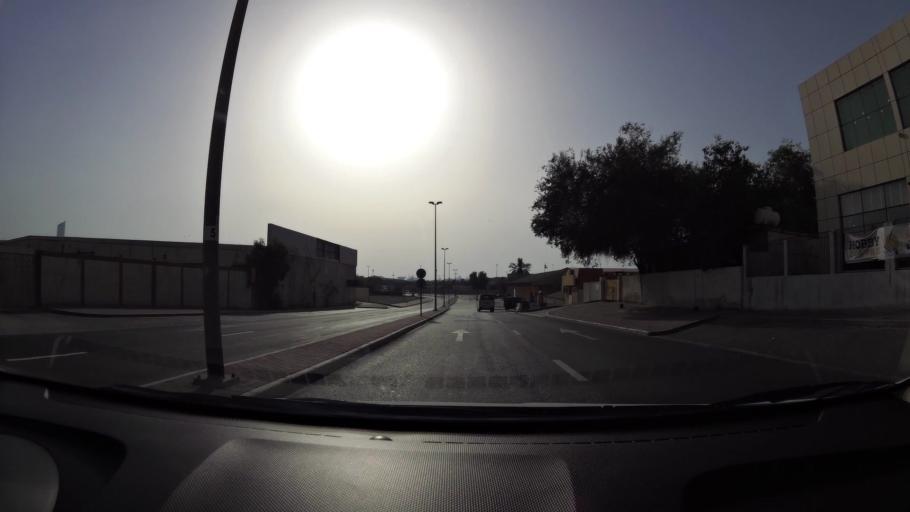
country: AE
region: Ash Shariqah
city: Sharjah
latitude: 25.2370
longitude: 55.3661
